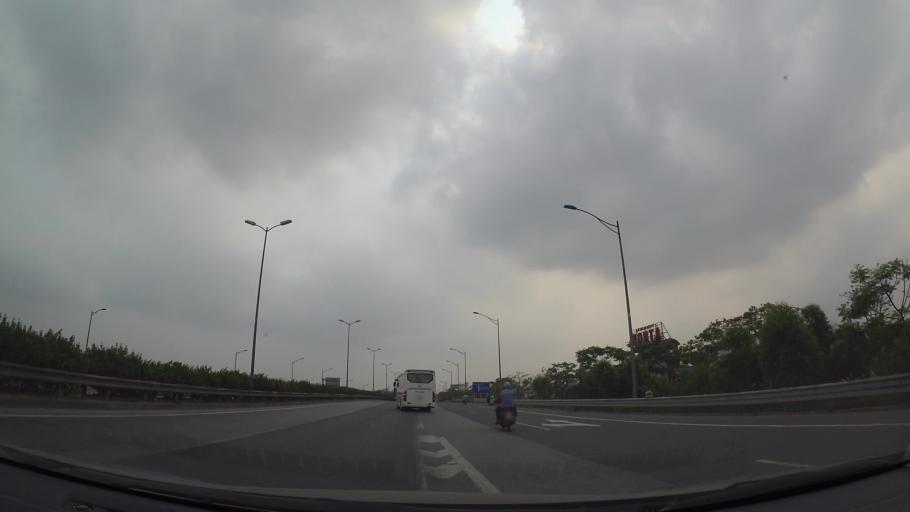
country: VN
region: Ha Noi
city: Trau Quy
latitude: 21.0095
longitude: 105.9157
